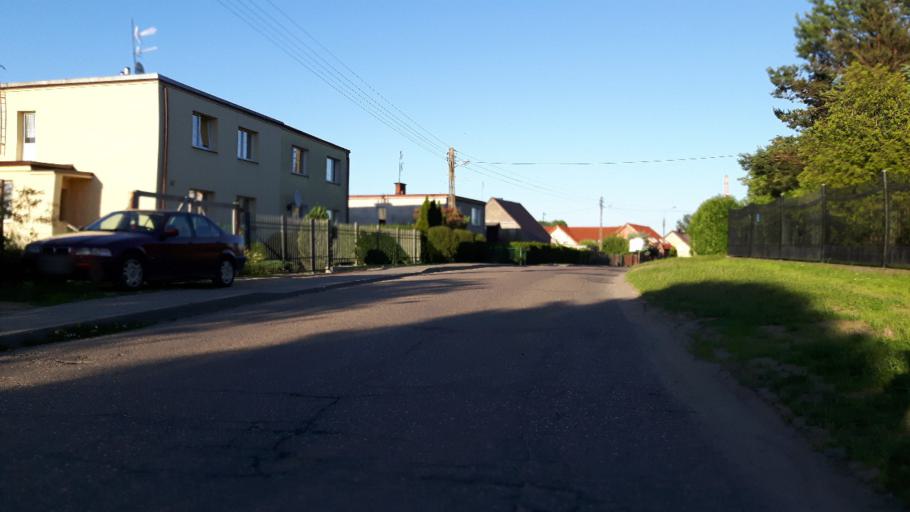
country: PL
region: Pomeranian Voivodeship
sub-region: Powiat pucki
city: Mosty
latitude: 54.6107
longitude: 18.5049
